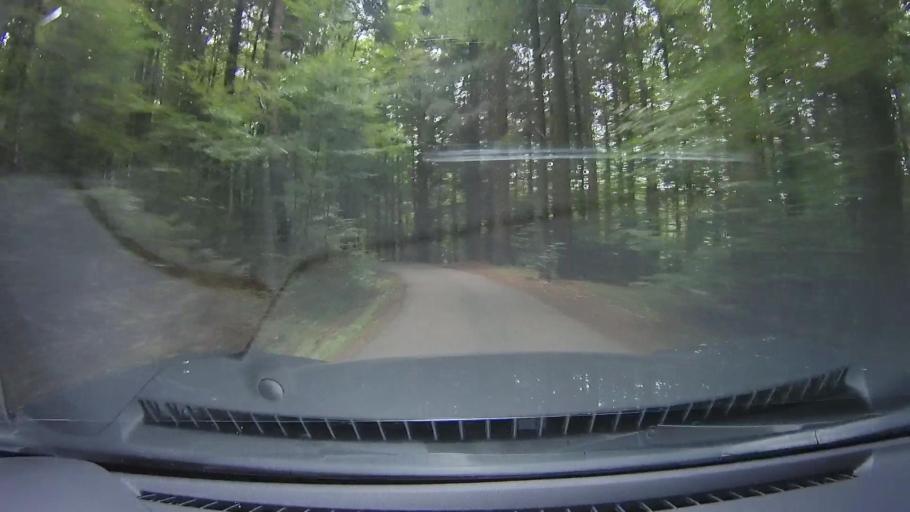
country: DE
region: Baden-Wuerttemberg
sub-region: Regierungsbezirk Stuttgart
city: Murrhardt
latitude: 48.9610
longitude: 9.5534
